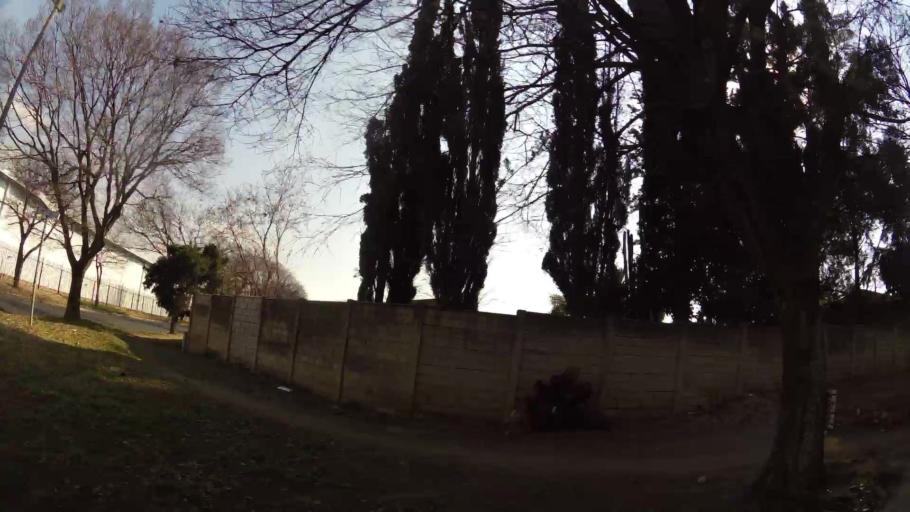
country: ZA
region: Gauteng
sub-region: Ekurhuleni Metropolitan Municipality
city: Boksburg
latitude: -26.1900
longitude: 28.2655
